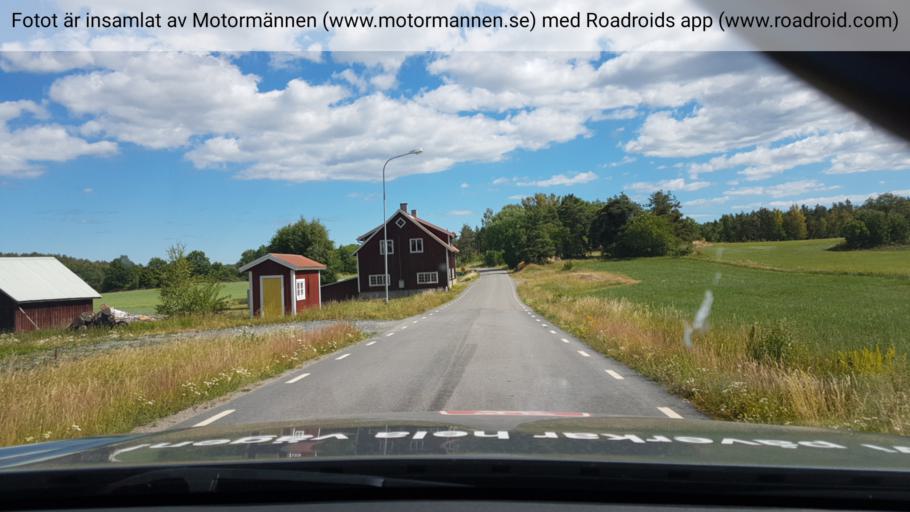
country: SE
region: Kalmar
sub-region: Vasterviks Kommun
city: Forserum
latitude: 58.0079
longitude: 16.5806
